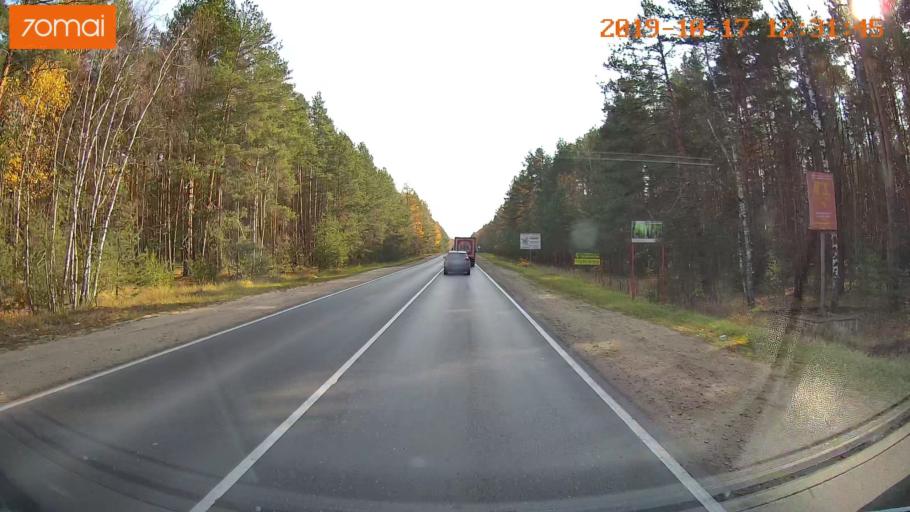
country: RU
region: Rjazan
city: Syntul
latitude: 54.9657
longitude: 41.3375
